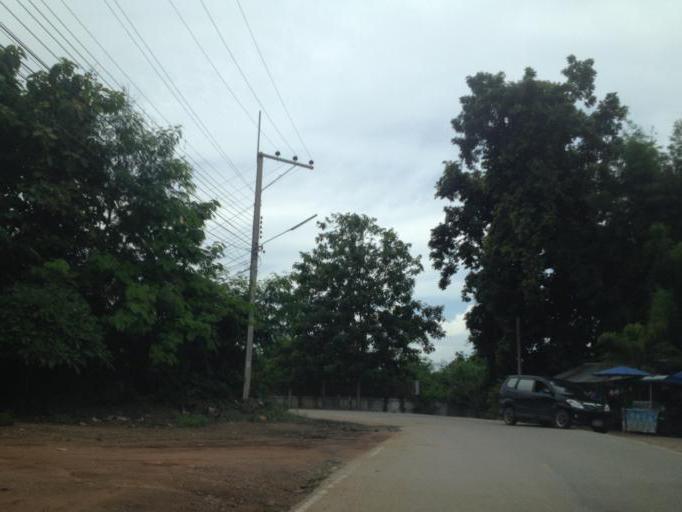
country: TH
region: Chiang Mai
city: Hang Dong
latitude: 18.6892
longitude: 98.8778
